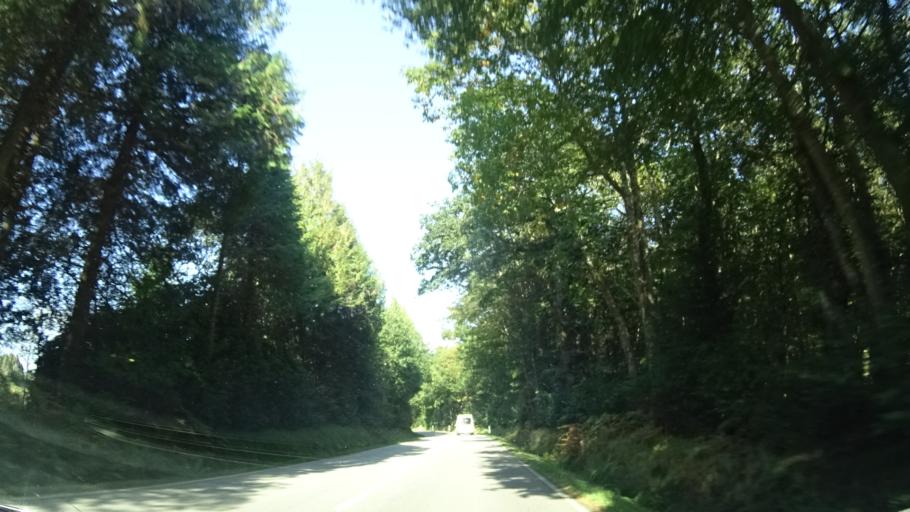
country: FR
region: Brittany
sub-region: Departement du Finistere
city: Cast
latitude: 48.1689
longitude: -4.1243
